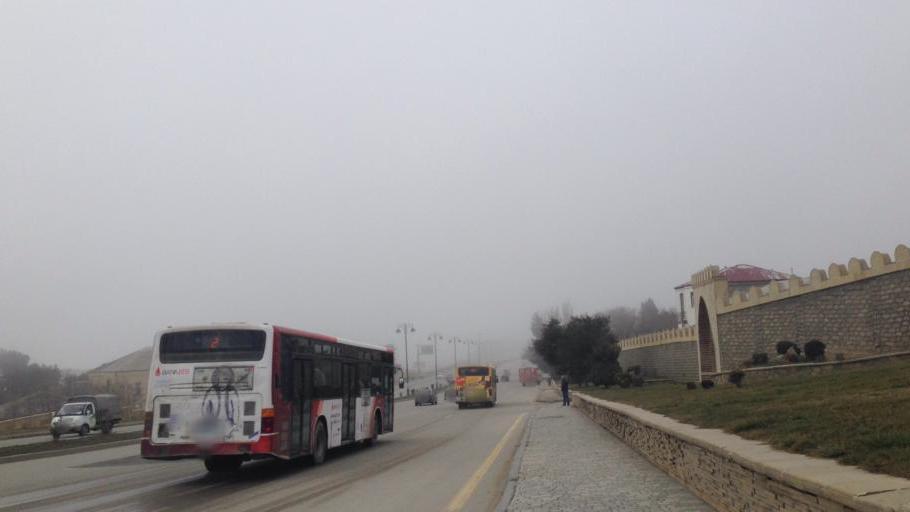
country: AZ
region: Baki
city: Qaracuxur
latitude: 40.3527
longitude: 49.9585
